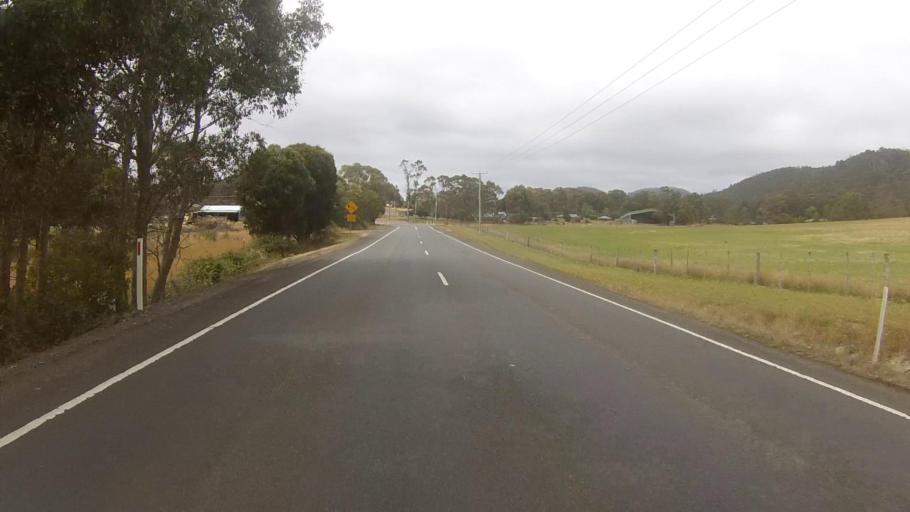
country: AU
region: Tasmania
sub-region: Kingborough
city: Margate
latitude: -42.9899
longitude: 147.1978
